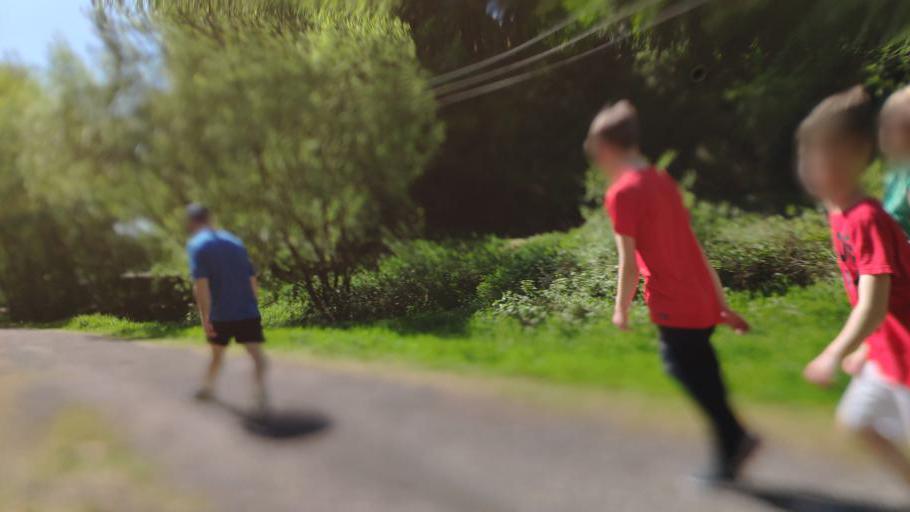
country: IE
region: Munster
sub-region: County Cork
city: Blarney
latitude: 51.9424
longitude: -8.5650
